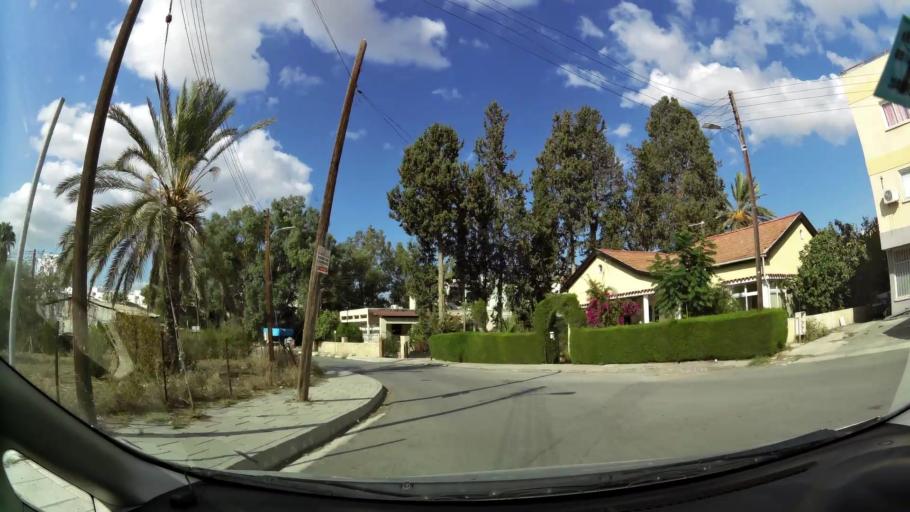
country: CY
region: Lefkosia
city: Nicosia
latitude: 35.1977
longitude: 33.3469
